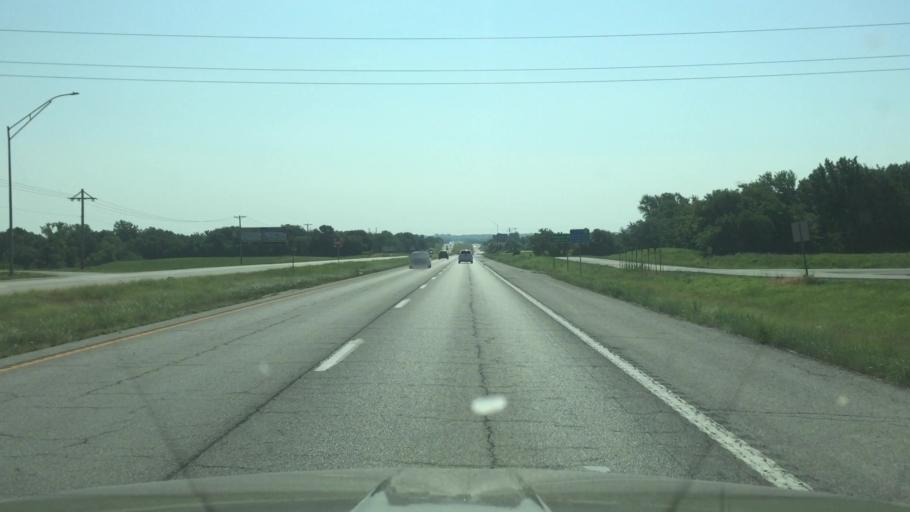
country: US
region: Missouri
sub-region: Johnson County
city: Warrensburg
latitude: 38.7738
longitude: -93.7063
